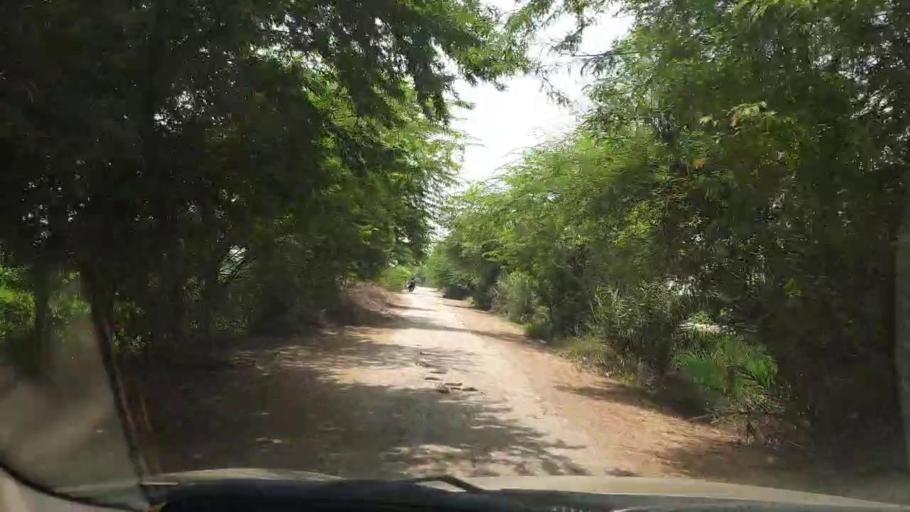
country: PK
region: Sindh
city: Larkana
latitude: 27.6111
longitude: 68.1330
